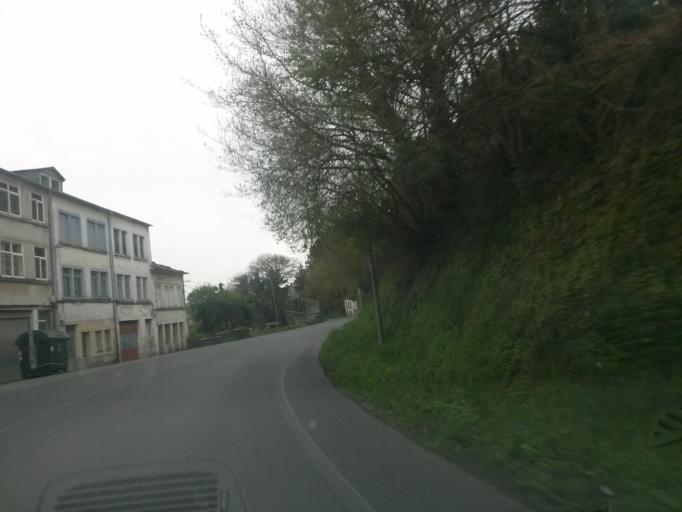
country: ES
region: Galicia
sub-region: Provincia de Lugo
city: Lugo
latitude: 43.0215
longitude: -7.5470
